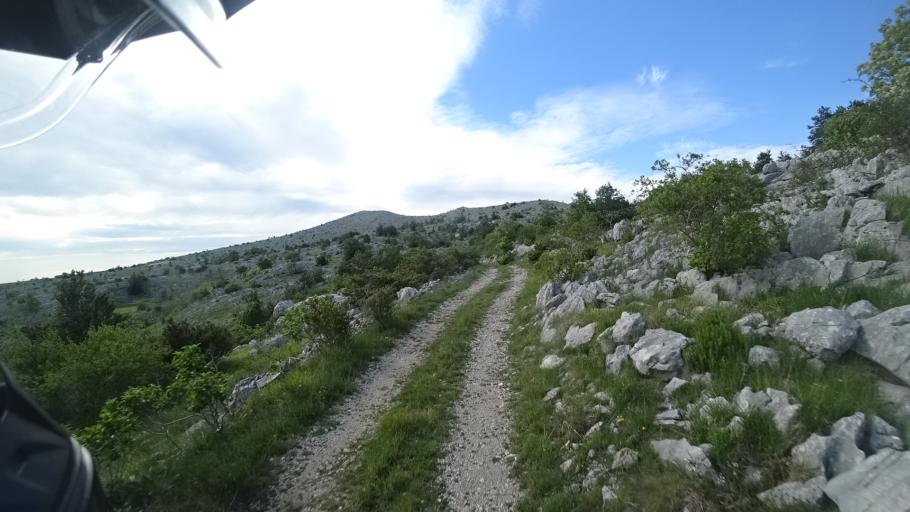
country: HR
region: Splitsko-Dalmatinska
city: Hrvace
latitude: 43.8007
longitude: 16.4324
